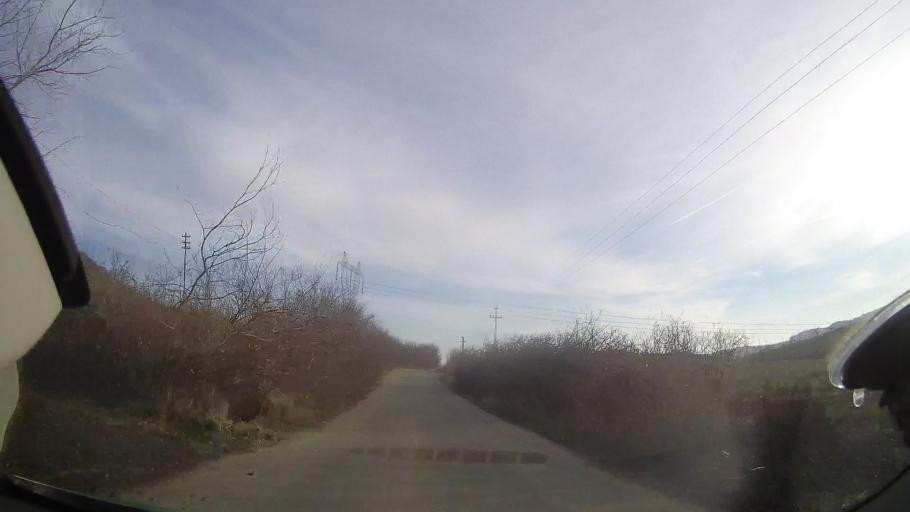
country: RO
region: Bihor
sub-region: Comuna Sarbi
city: Sarbi
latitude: 47.1827
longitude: 22.1321
